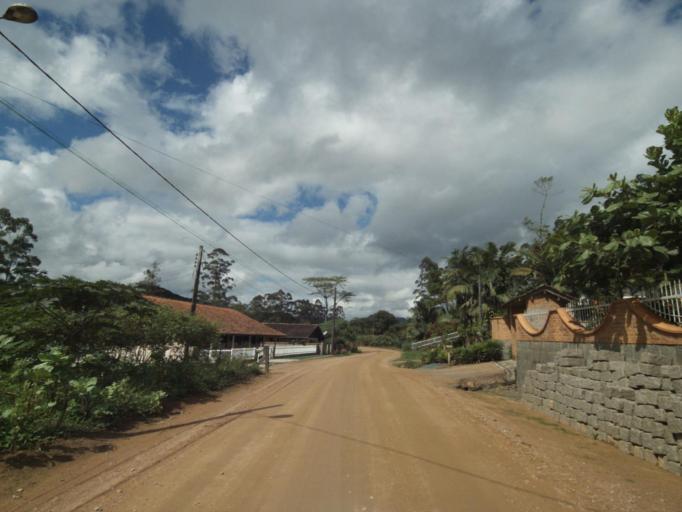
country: BR
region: Santa Catarina
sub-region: Pomerode
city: Pomerode
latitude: -26.6916
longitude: -49.1769
